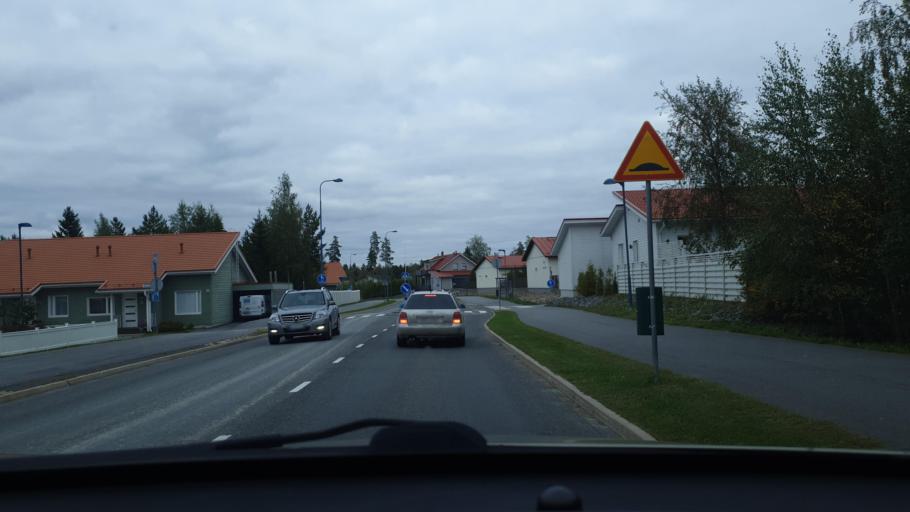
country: FI
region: Ostrobothnia
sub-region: Vaasa
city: Korsholm
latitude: 63.1249
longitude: 21.6614
